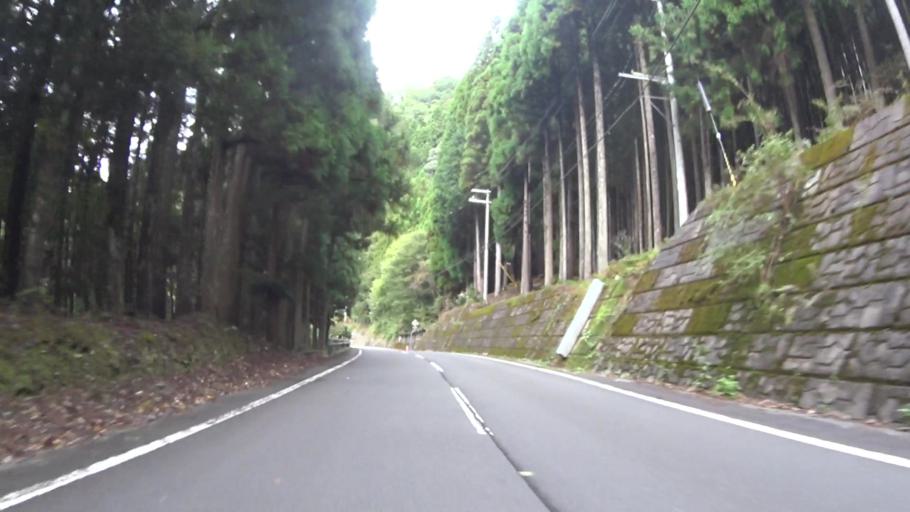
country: JP
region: Fukui
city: Obama
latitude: 35.3209
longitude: 135.6903
